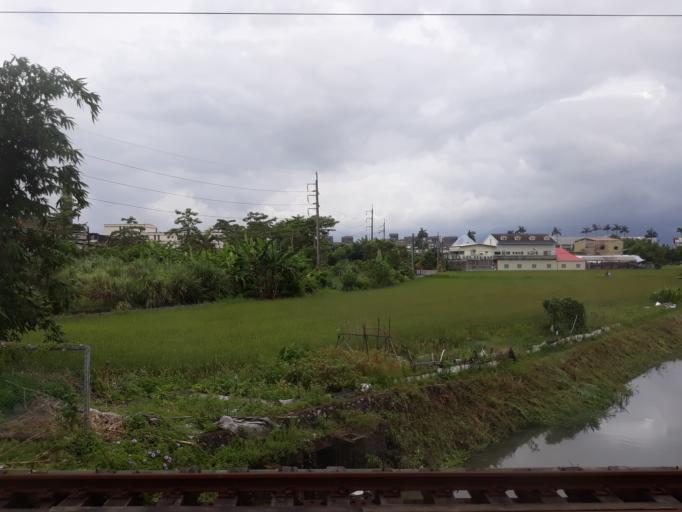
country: TW
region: Taiwan
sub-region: Yilan
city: Yilan
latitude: 24.6984
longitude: 121.7752
